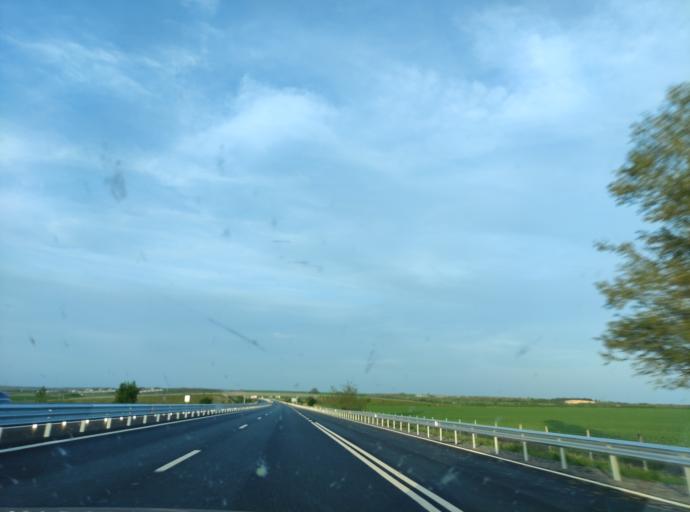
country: BG
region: Stara Zagora
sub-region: Obshtina Chirpan
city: Chirpan
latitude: 42.1958
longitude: 25.2526
